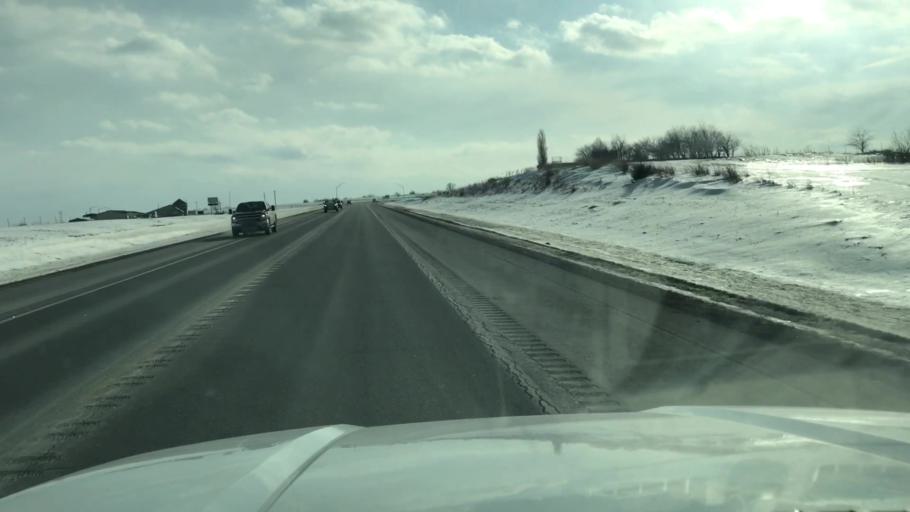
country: US
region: Missouri
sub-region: Nodaway County
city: Maryville
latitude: 40.3380
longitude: -94.8535
